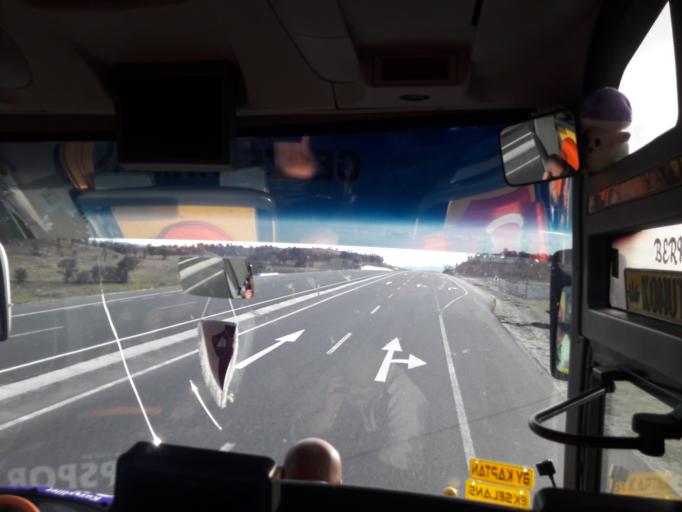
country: TR
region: Cankiri
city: Ilgaz
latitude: 40.8557
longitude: 33.6095
